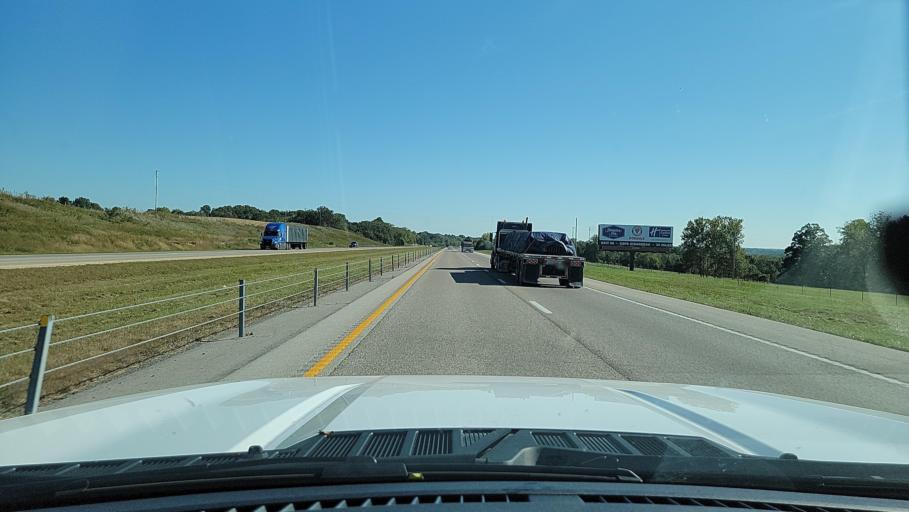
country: US
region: Missouri
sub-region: Perry County
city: Perryville
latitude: 37.7490
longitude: -89.9154
